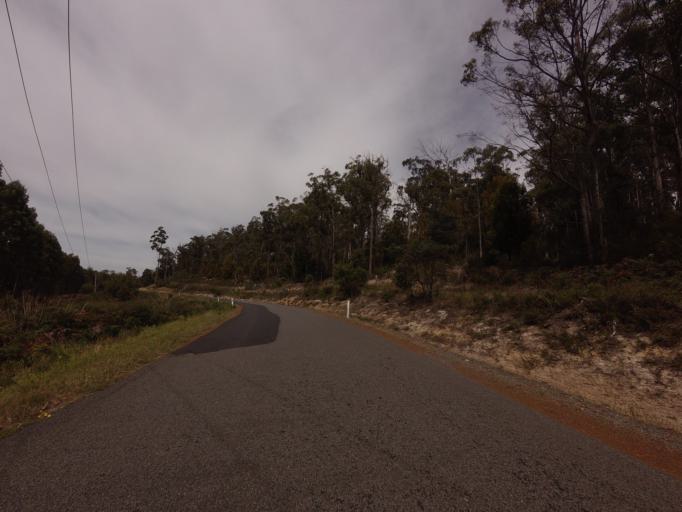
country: AU
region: Tasmania
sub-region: Sorell
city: Sorell
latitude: -42.5839
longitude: 147.5582
